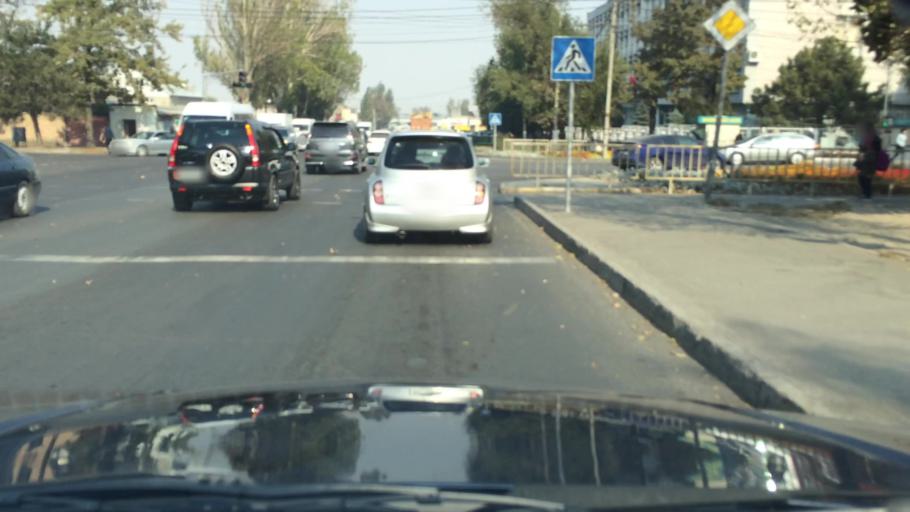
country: KG
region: Chuy
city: Lebedinovka
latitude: 42.8832
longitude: 74.6367
